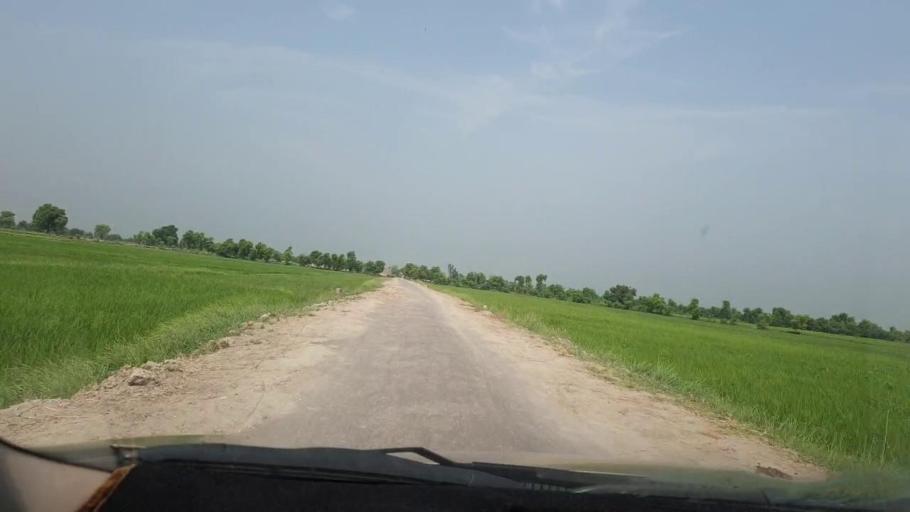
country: PK
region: Sindh
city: Goth Garelo
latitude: 27.4844
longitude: 68.0481
